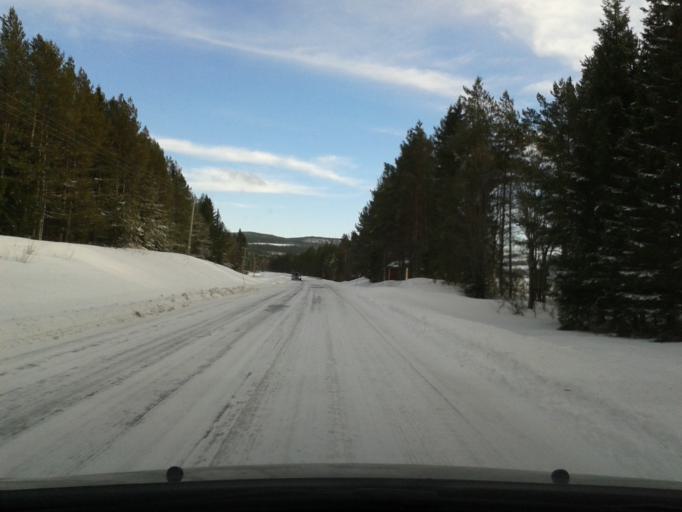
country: SE
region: Vaesterbotten
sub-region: Asele Kommun
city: Asele
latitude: 64.3419
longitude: 17.0163
